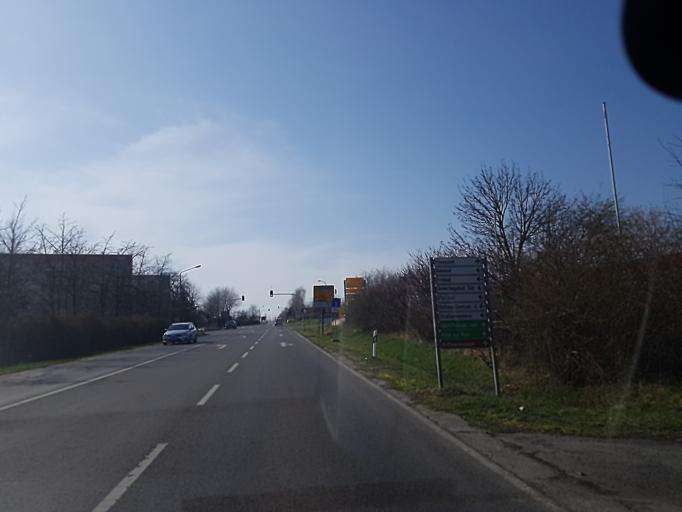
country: DE
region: Brandenburg
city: Calau
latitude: 51.7481
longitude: 13.9555
